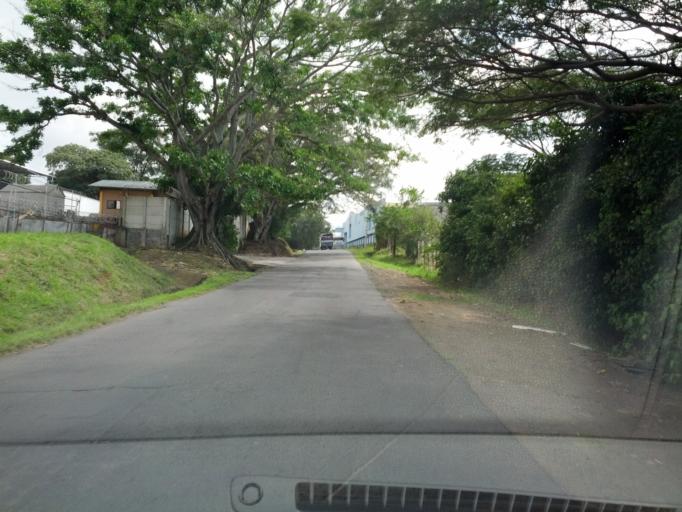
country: CR
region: Alajuela
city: Alajuela
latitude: 9.9877
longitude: -84.2234
